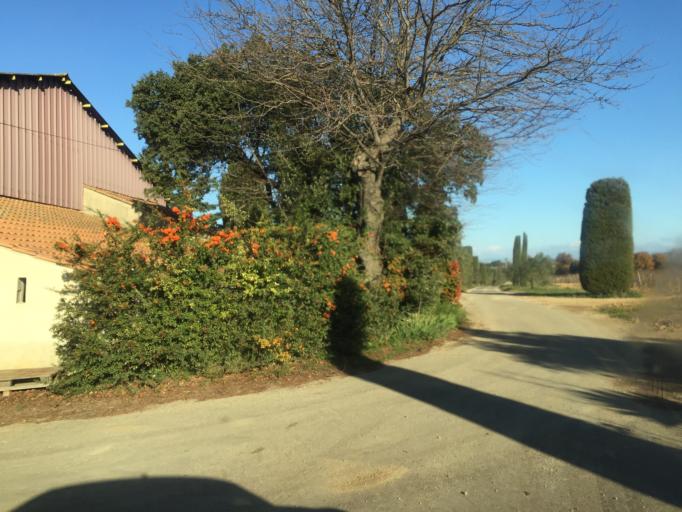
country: FR
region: Provence-Alpes-Cote d'Azur
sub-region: Departement du Vaucluse
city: Bedarrides
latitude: 44.0307
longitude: 4.8888
